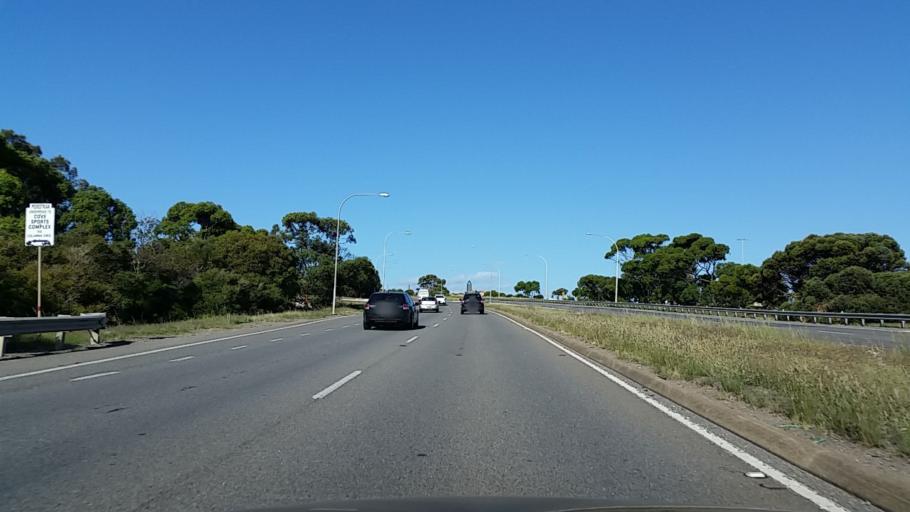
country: AU
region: South Australia
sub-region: Onkaparinga
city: Reynella
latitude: -35.0856
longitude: 138.5050
